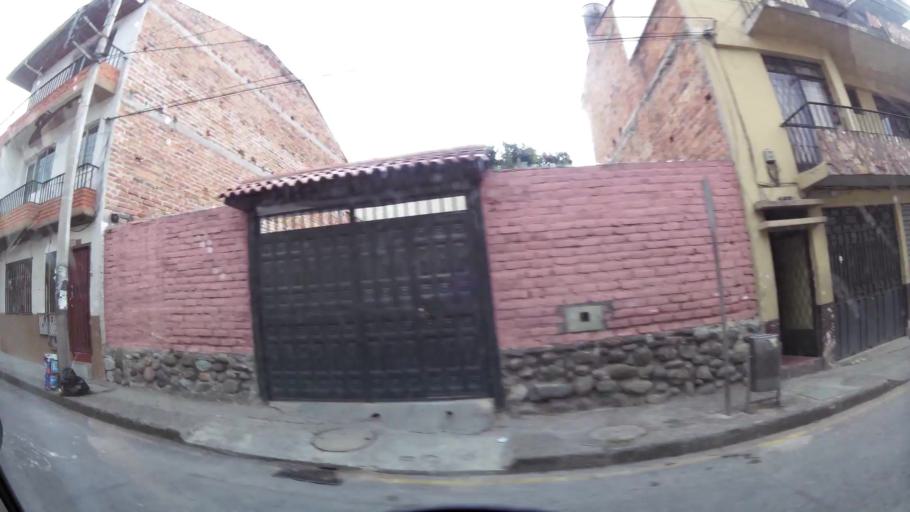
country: EC
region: Azuay
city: Cuenca
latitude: -2.8903
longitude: -79.0136
